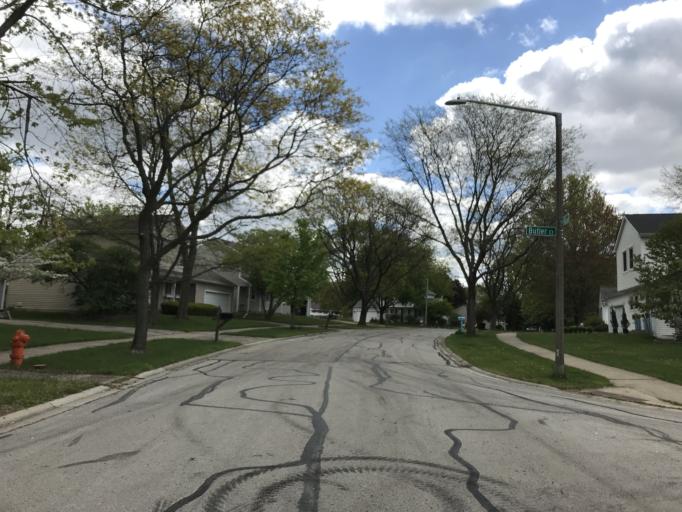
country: US
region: Illinois
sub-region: Will County
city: Bolingbrook
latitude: 41.7392
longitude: -88.1061
